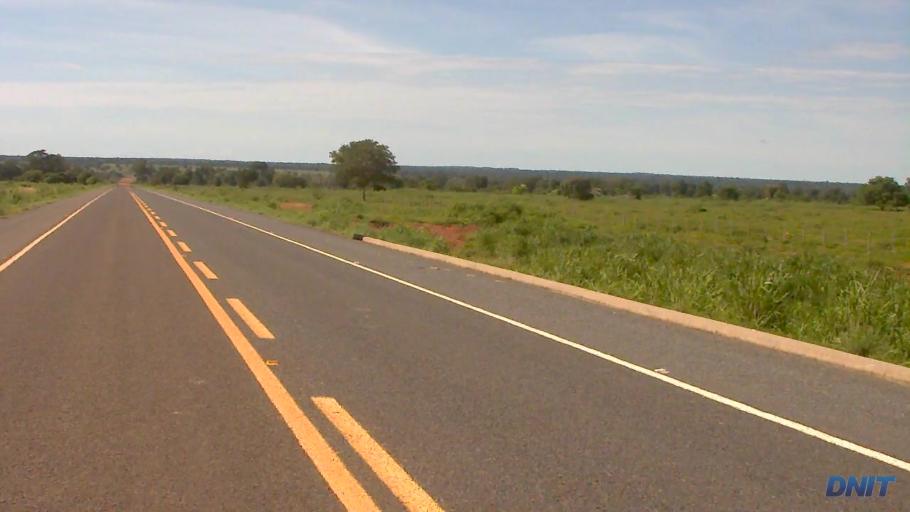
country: BR
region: Goias
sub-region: Sao Miguel Do Araguaia
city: Sao Miguel do Araguaia
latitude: -13.4874
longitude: -50.1100
